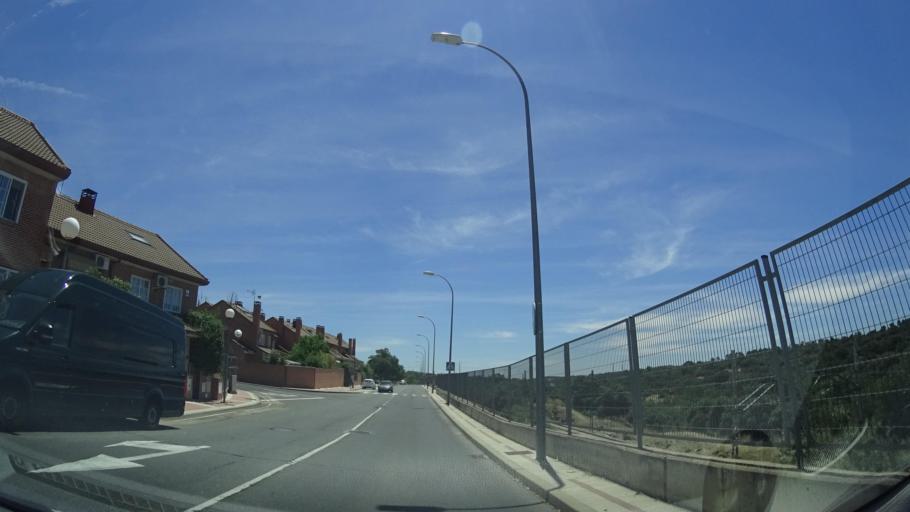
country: ES
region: Madrid
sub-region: Provincia de Madrid
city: Collado-Villalba
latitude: 40.6229
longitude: -3.9976
